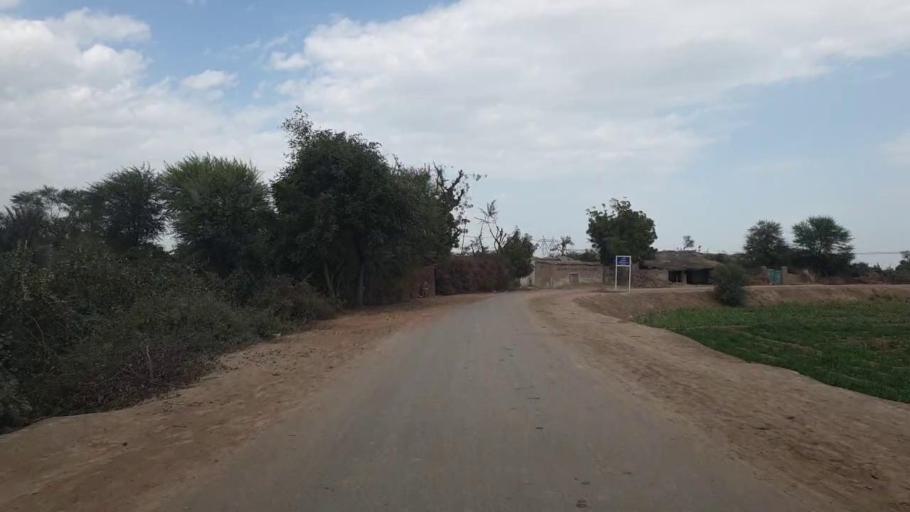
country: PK
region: Sindh
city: Hala
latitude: 25.9790
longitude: 68.4061
